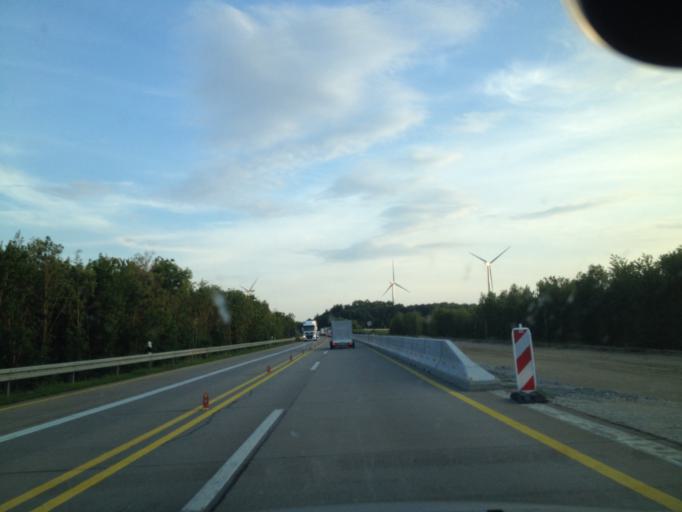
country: DE
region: Bavaria
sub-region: Regierungsbezirk Mittelfranken
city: Gollhofen
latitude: 49.5618
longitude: 10.1677
